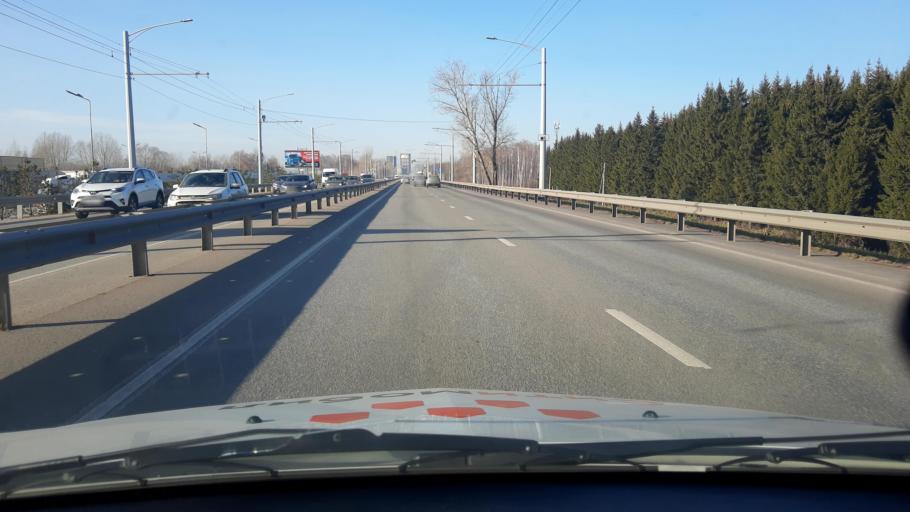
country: RU
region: Bashkortostan
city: Ufa
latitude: 54.7654
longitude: 55.9402
